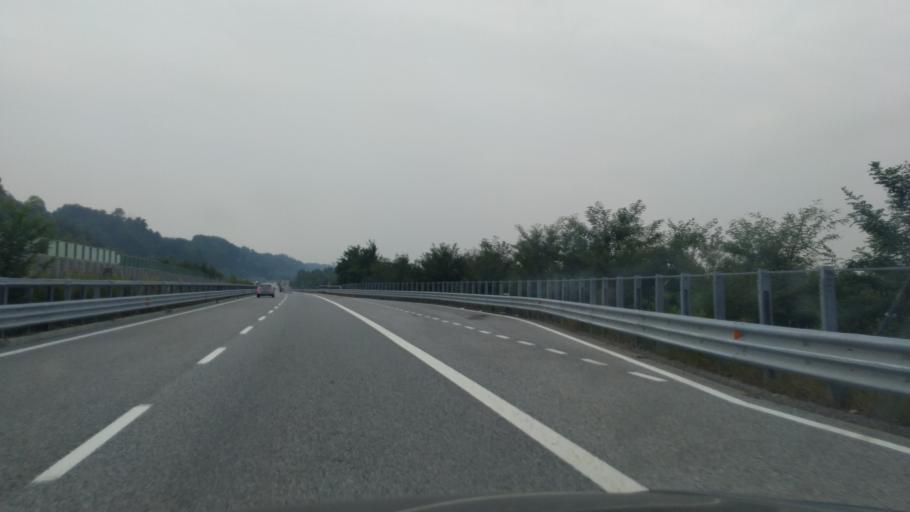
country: IT
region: Piedmont
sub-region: Provincia di Cuneo
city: Montanera
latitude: 44.4666
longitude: 7.6673
